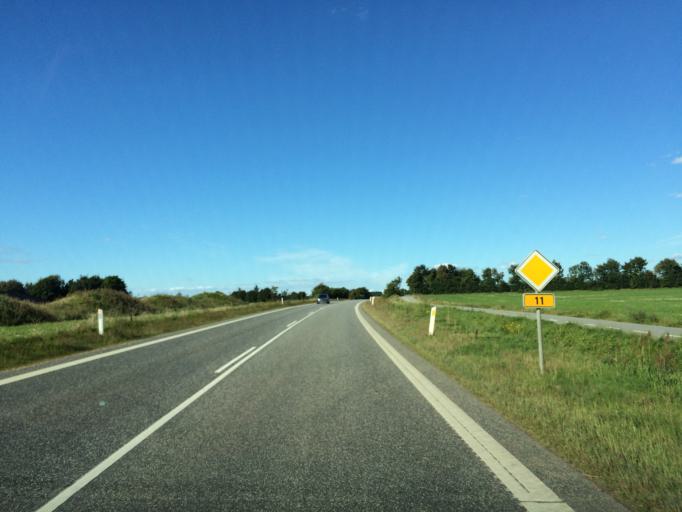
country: DK
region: Central Jutland
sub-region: Holstebro Kommune
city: Holstebro
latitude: 56.3093
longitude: 8.6042
